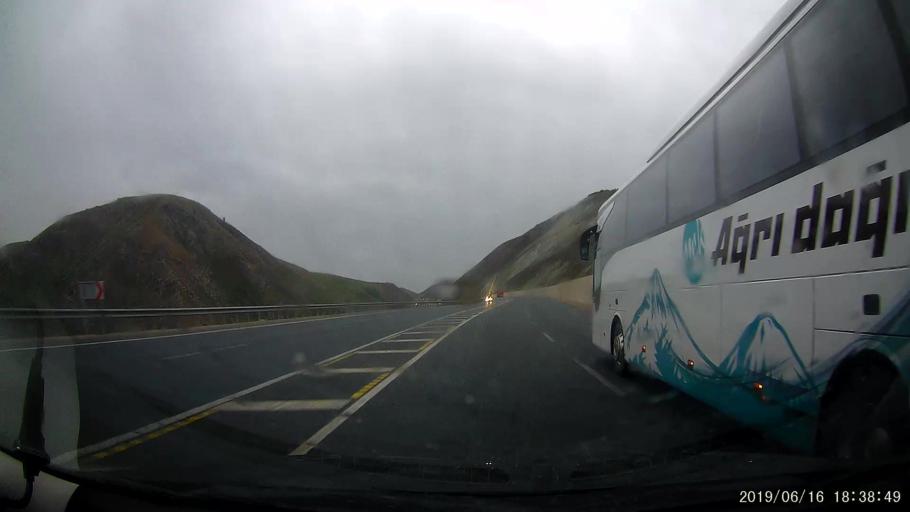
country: TR
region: Erzincan
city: Catalarmut
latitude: 39.8829
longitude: 39.1768
